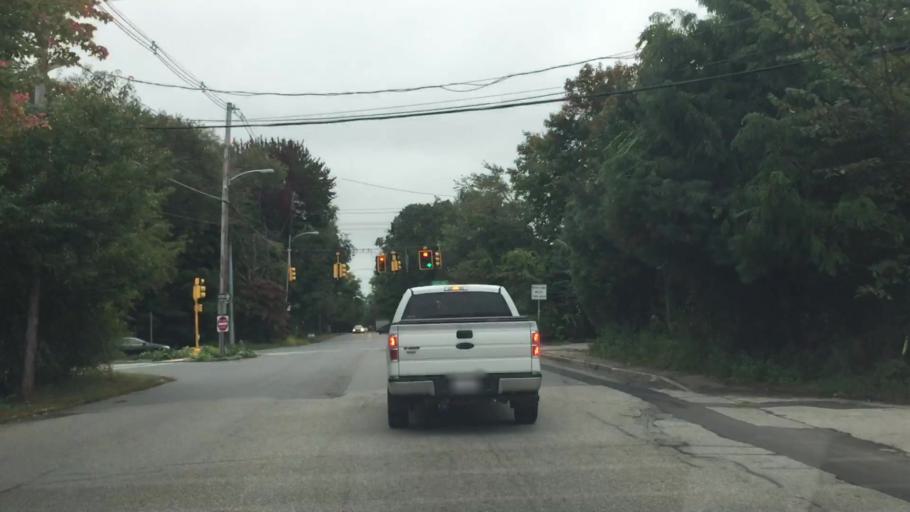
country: US
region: Massachusetts
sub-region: Essex County
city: North Andover
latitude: 42.6880
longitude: -71.1223
